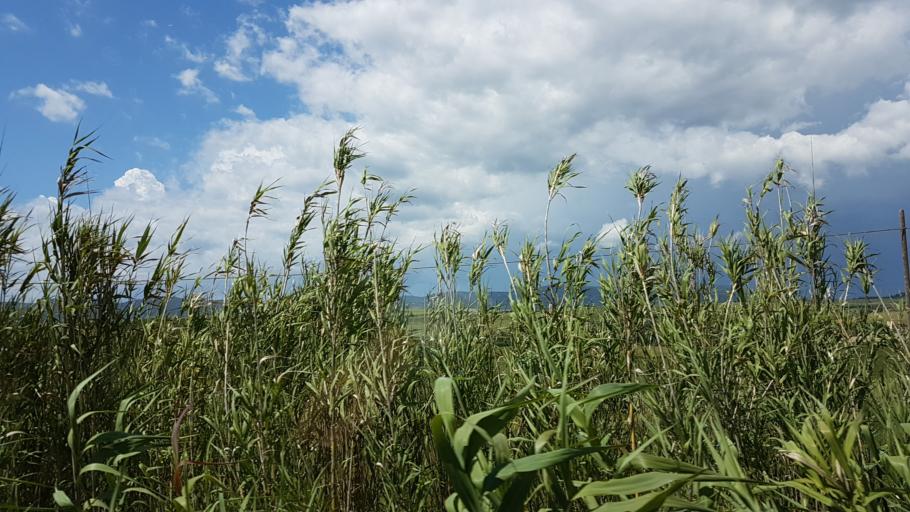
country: IT
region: Tuscany
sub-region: Province of Pisa
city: Orciano Pisano
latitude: 43.4551
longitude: 10.5231
